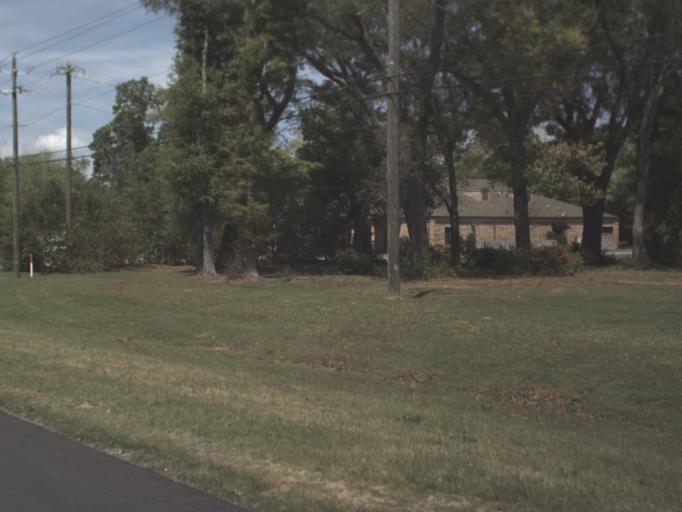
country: US
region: Florida
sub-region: Escambia County
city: Ensley
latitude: 30.5327
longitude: -87.2419
